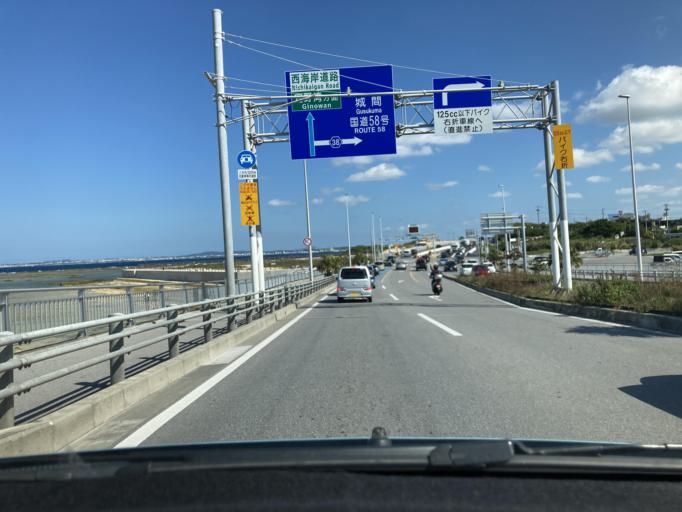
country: JP
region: Okinawa
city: Ginowan
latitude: 26.2711
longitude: 127.7059
